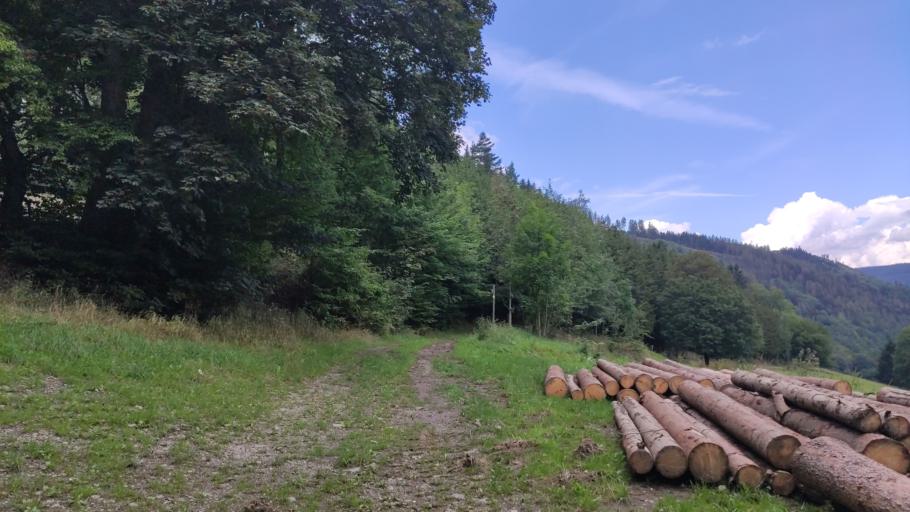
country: DE
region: Thuringia
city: Leutenberg
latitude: 50.5712
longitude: 11.4433
